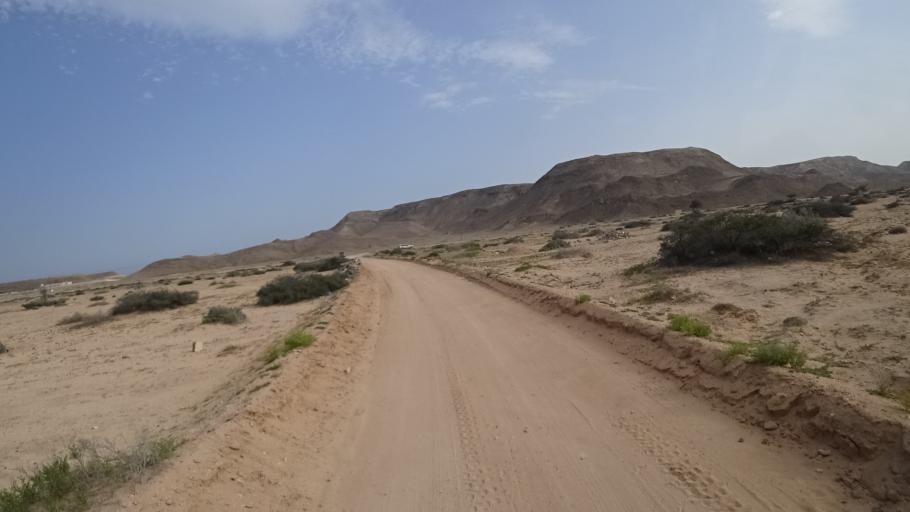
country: OM
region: Ash Sharqiyah
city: Sur
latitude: 22.4367
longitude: 59.8175
